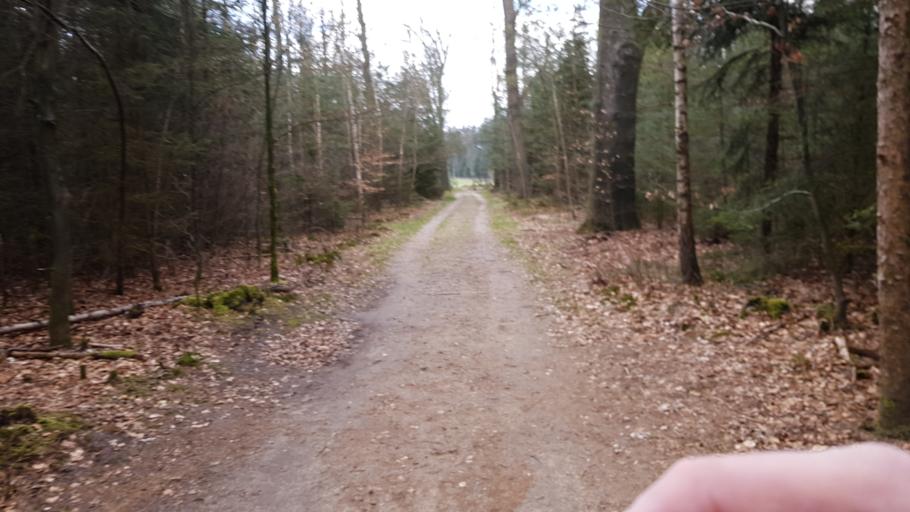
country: NL
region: Gelderland
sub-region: Gemeente Epe
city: Vaassen
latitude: 52.3028
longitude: 5.9297
